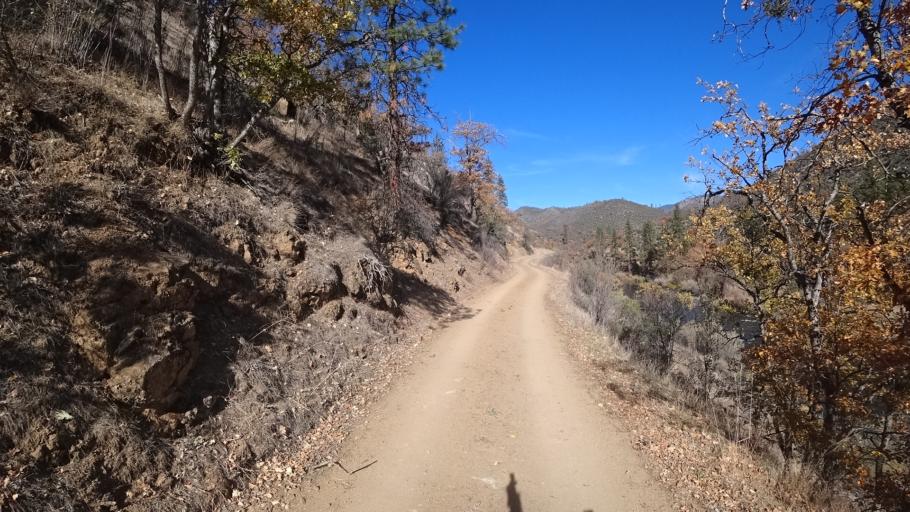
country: US
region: California
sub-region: Siskiyou County
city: Yreka
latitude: 41.8643
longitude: -122.7373
